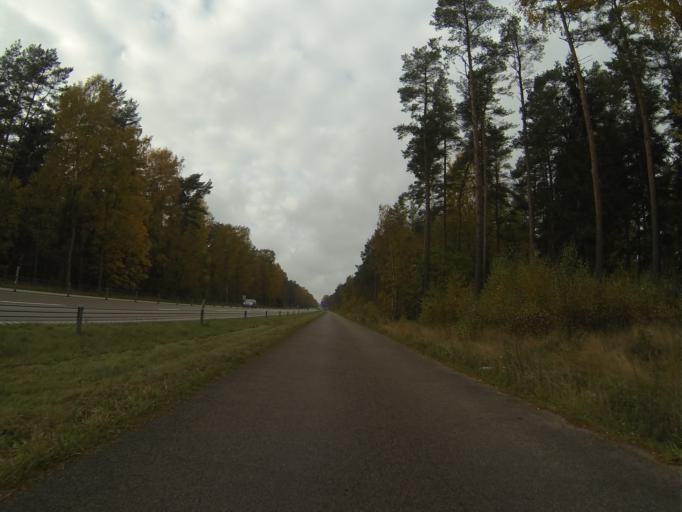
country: SE
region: Skane
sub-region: Sjobo Kommun
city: Sjoebo
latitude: 55.6371
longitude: 13.6599
